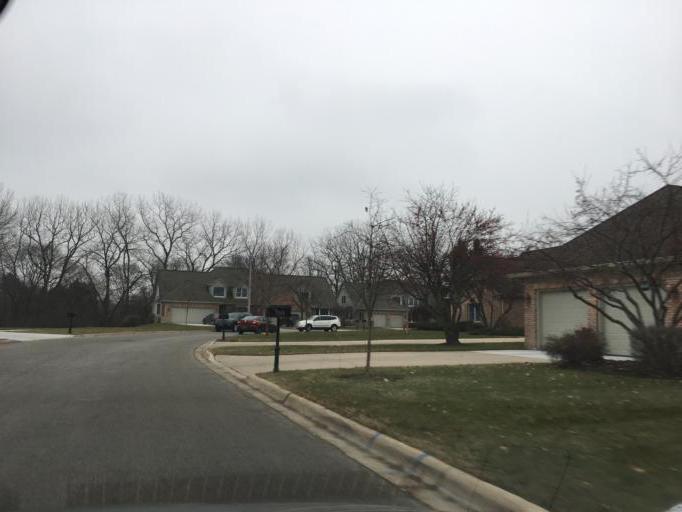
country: US
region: Illinois
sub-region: McHenry County
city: Lakewood
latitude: 42.2254
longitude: -88.3564
